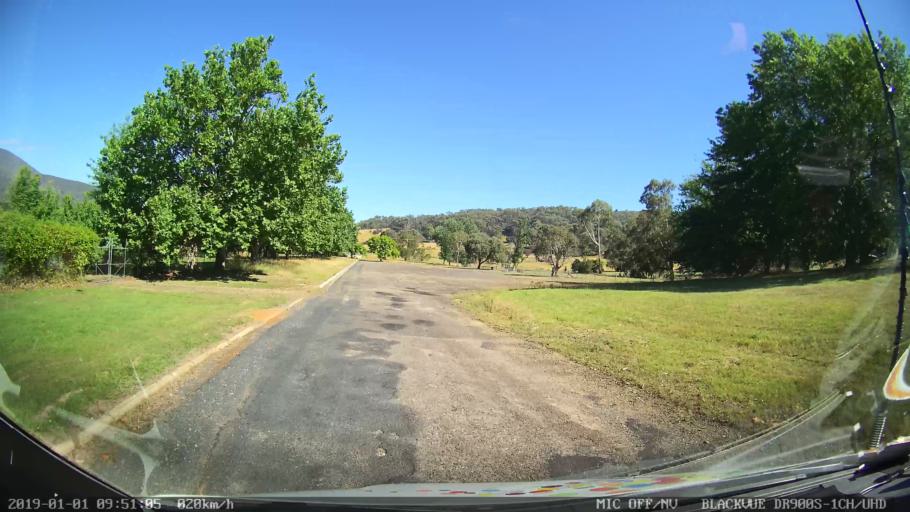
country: AU
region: New South Wales
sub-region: Snowy River
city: Jindabyne
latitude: -36.2154
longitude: 148.1243
